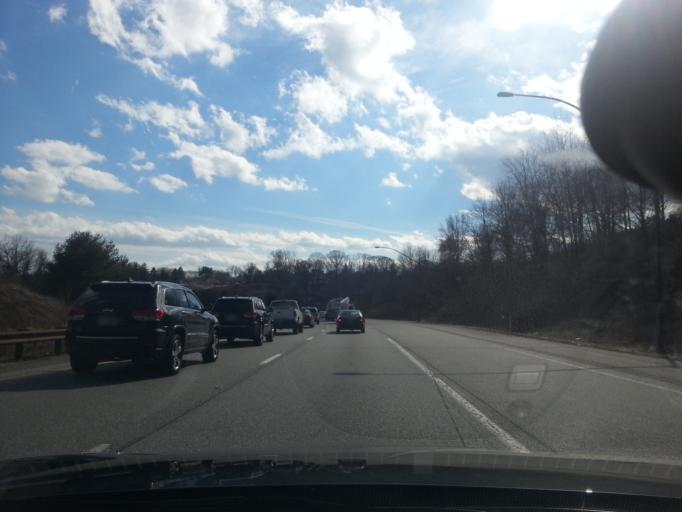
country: US
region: Pennsylvania
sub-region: Delaware County
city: Broomall
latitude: 39.9776
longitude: -75.3409
